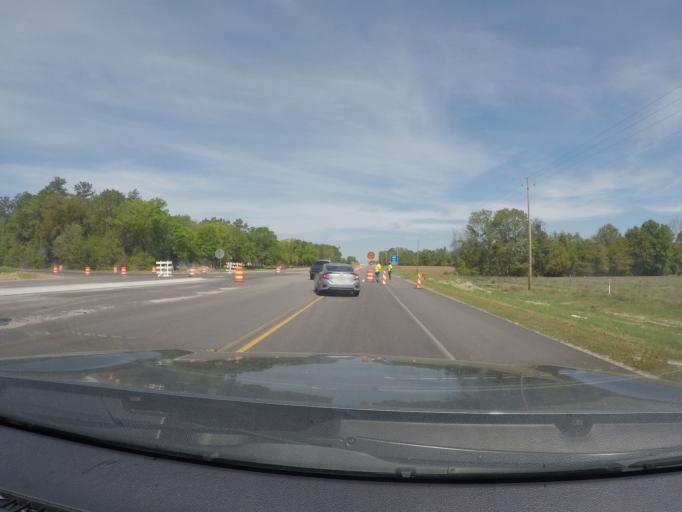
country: US
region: Georgia
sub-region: Bulloch County
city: Brooklet
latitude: 32.2727
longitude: -81.7205
